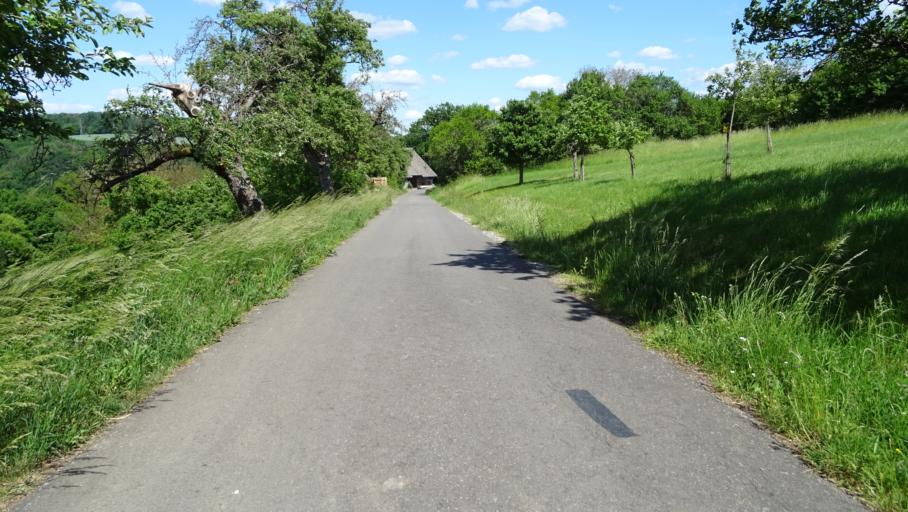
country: DE
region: Baden-Wuerttemberg
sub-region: Karlsruhe Region
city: Seckach
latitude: 49.4307
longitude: 9.3662
